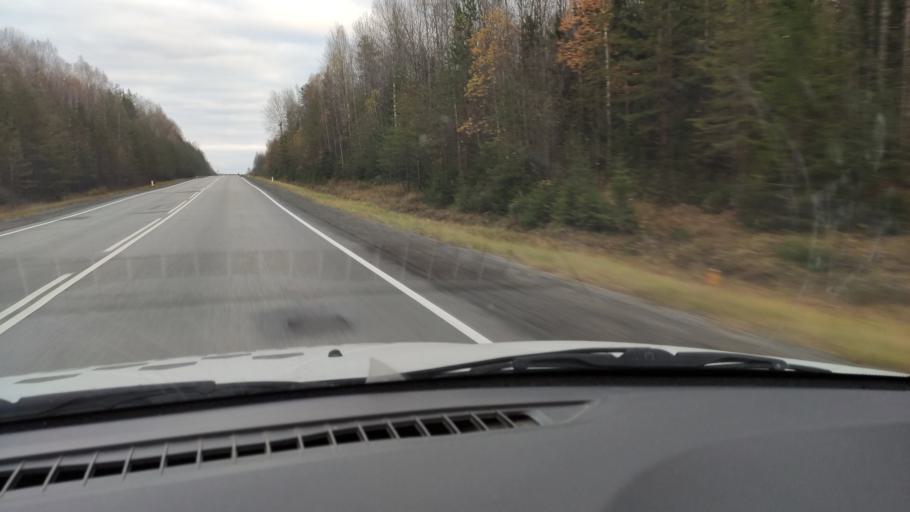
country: RU
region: Kirov
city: Chernaya Kholunitsa
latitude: 58.8617
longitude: 51.6061
